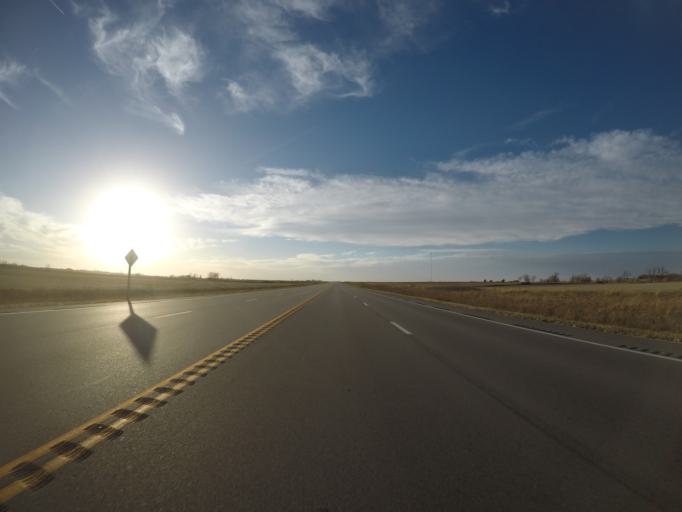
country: US
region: Kansas
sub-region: Chase County
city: Cottonwood Falls
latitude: 38.4050
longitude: -96.4012
